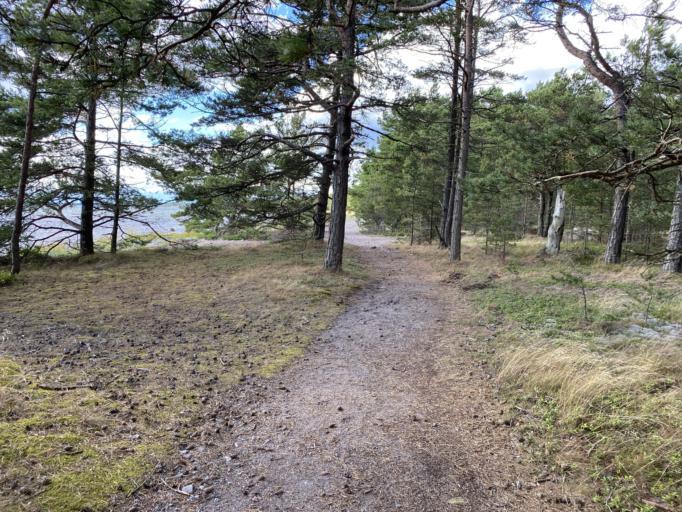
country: SE
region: Stockholm
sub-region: Varmdo Kommun
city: Holo
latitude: 59.2756
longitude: 18.9146
